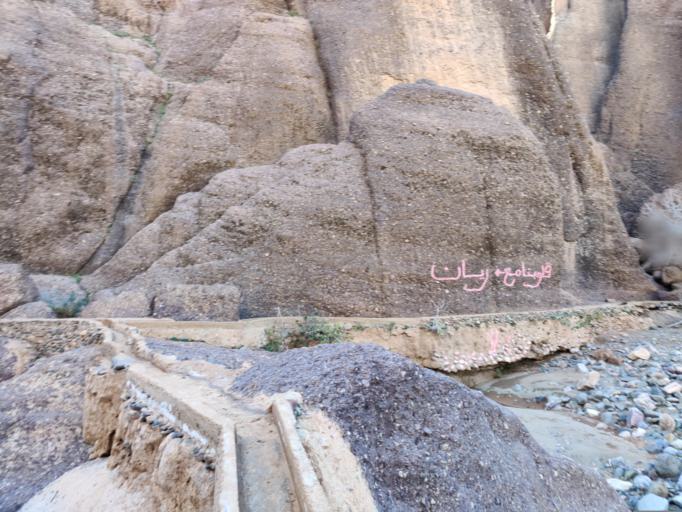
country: MA
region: Souss-Massa-Draa
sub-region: Taroudannt
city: Taliouine
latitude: 30.5550
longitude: -7.5925
